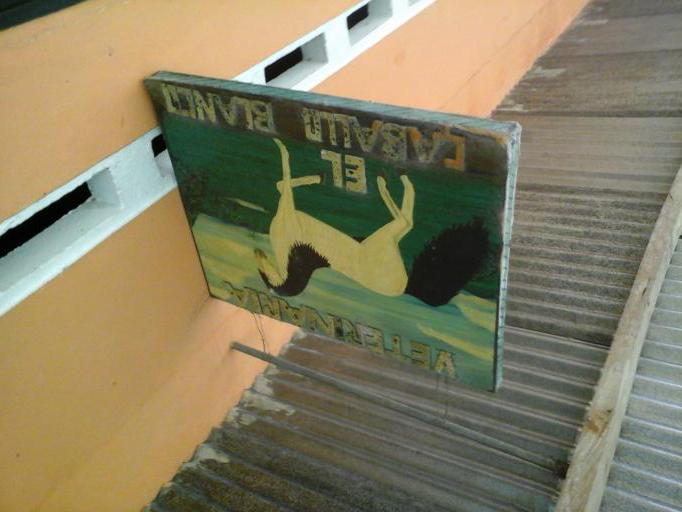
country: CO
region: Caqueta
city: El Doncello
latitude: 1.6124
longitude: -74.9946
